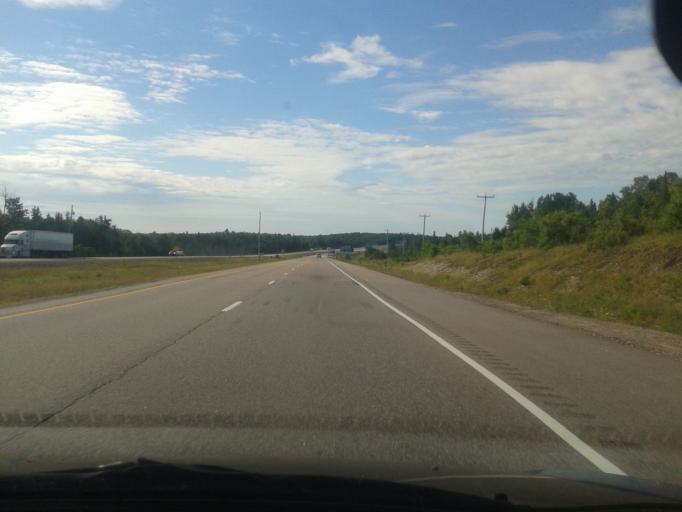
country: CA
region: Ontario
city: South River
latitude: 45.8830
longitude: -79.3792
